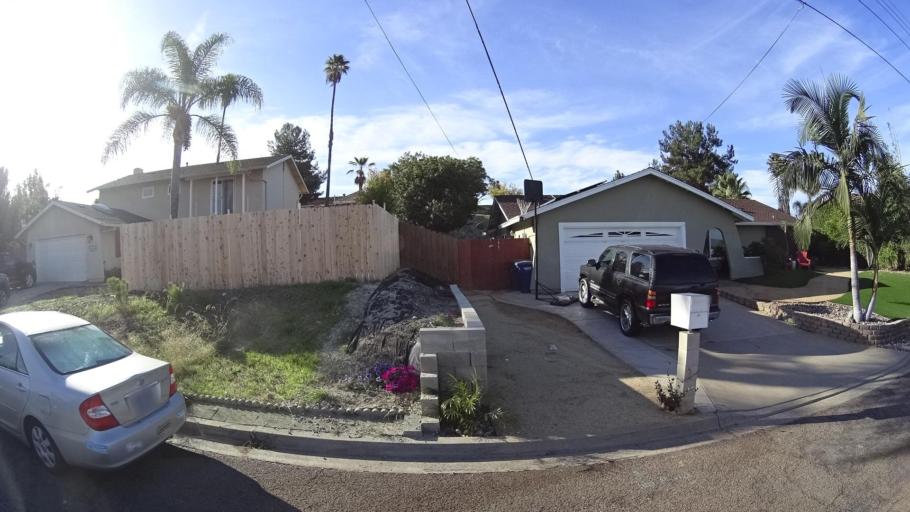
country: US
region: California
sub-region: San Diego County
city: Spring Valley
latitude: 32.7392
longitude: -116.9774
